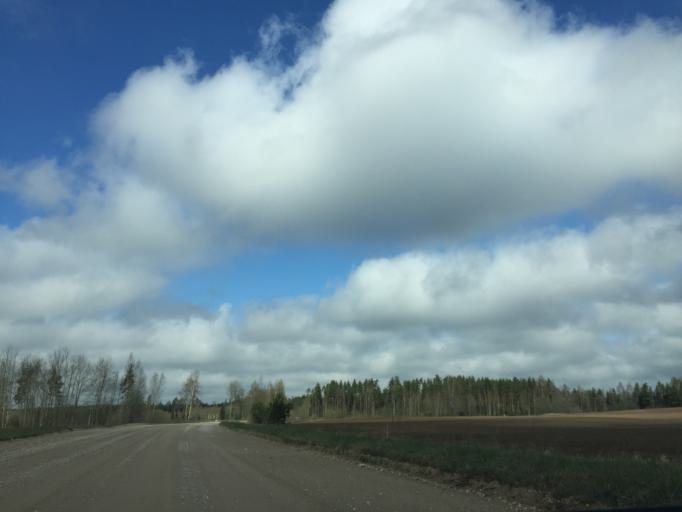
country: LV
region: Apes Novads
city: Ape
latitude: 57.4858
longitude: 26.4297
